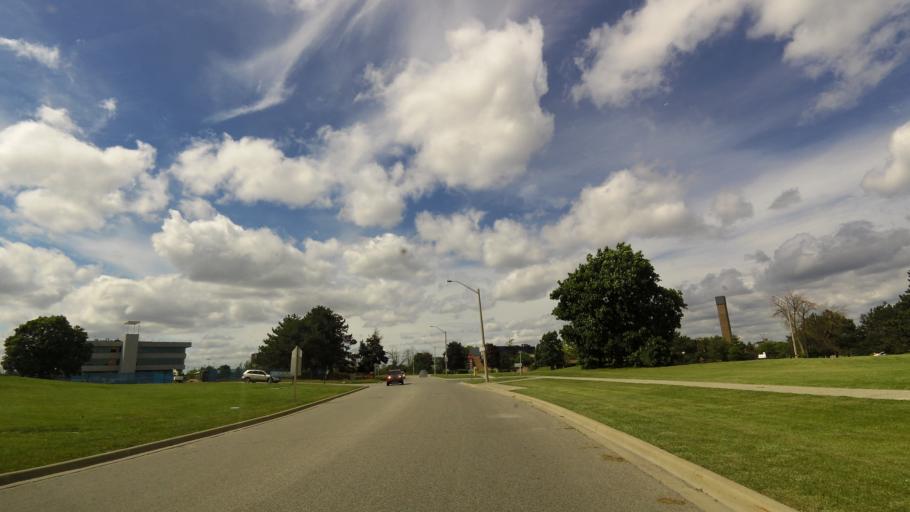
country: CA
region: Ontario
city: Mississauga
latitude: 43.5217
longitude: -79.6574
